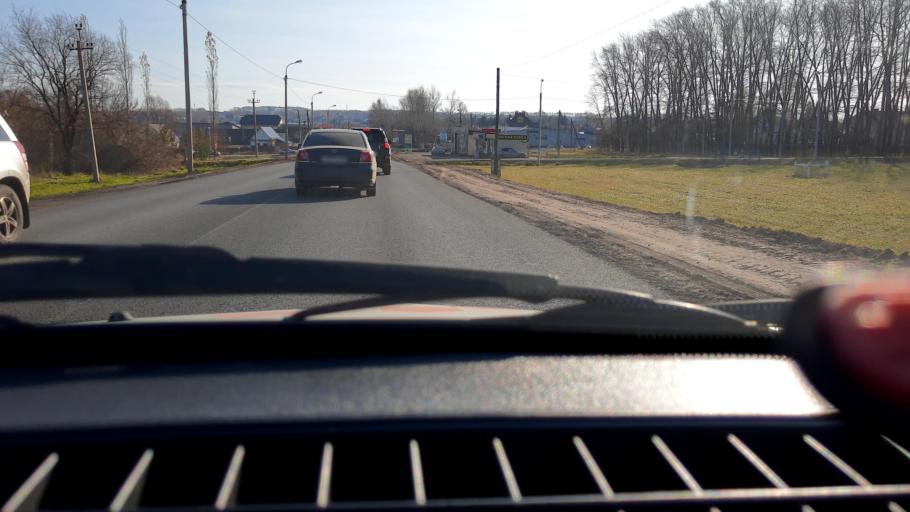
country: RU
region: Bashkortostan
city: Kabakovo
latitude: 54.6274
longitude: 56.1025
